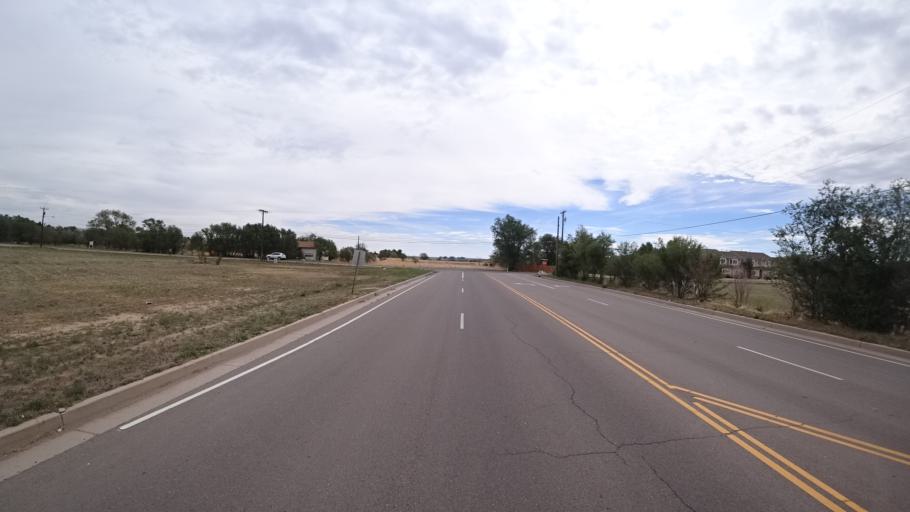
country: US
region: Colorado
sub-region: El Paso County
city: Fountain
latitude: 38.6959
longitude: -104.6977
